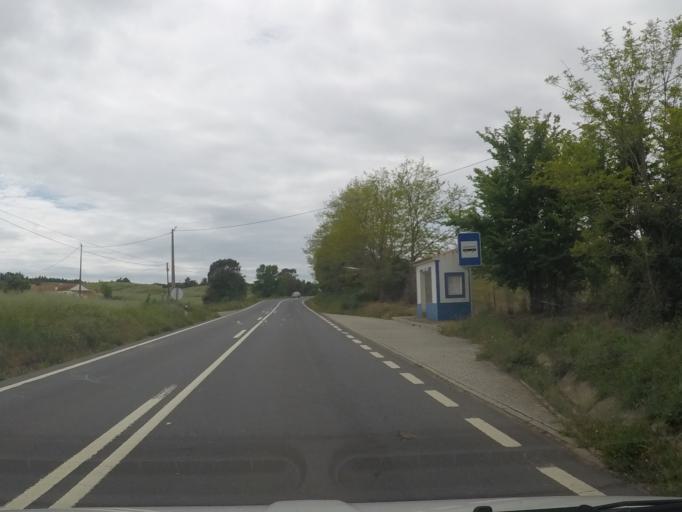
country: PT
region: Setubal
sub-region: Santiago do Cacem
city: Cercal
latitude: 37.8237
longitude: -8.6915
